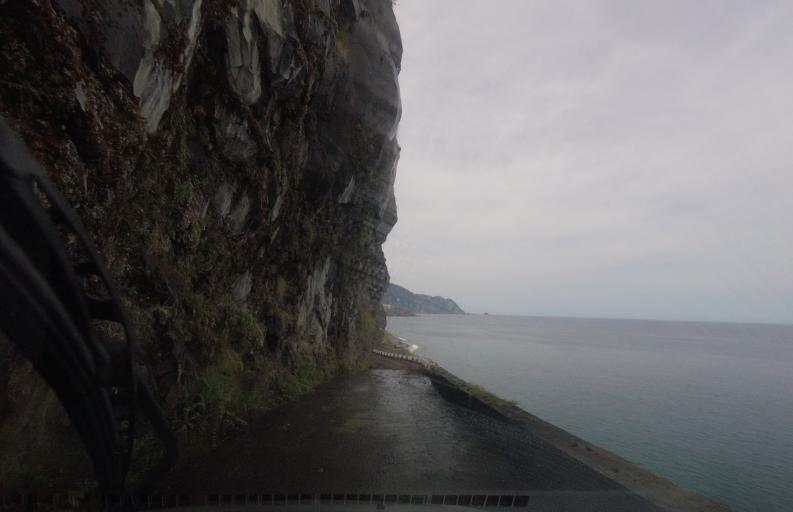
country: PT
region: Madeira
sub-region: Sao Vicente
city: Sao Vicente
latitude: 32.8134
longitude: -17.0746
